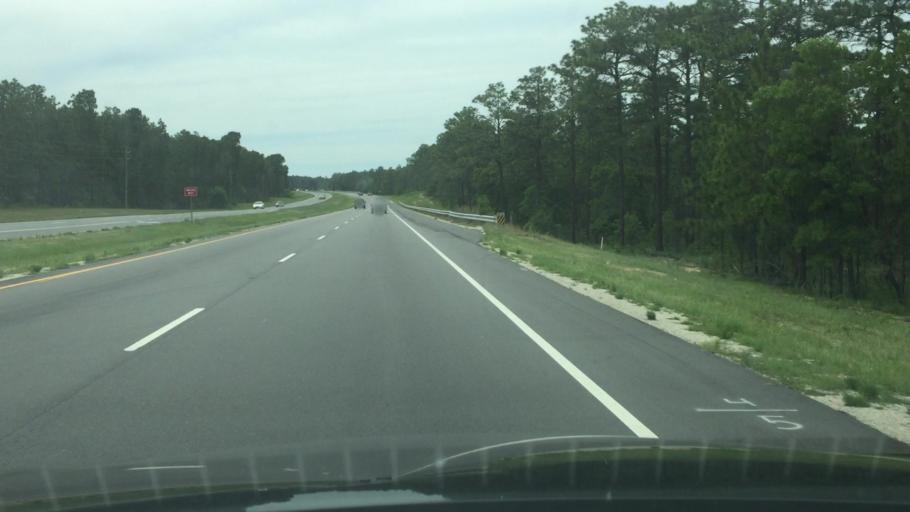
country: US
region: North Carolina
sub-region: Cumberland County
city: Spring Lake
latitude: 35.2242
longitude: -79.0080
